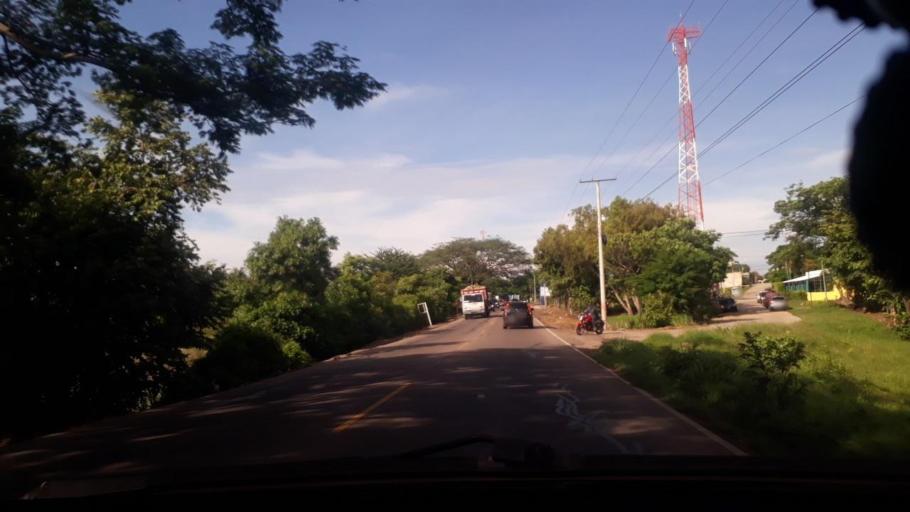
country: GT
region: Jutiapa
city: El Progreso
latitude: 14.3239
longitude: -89.8617
